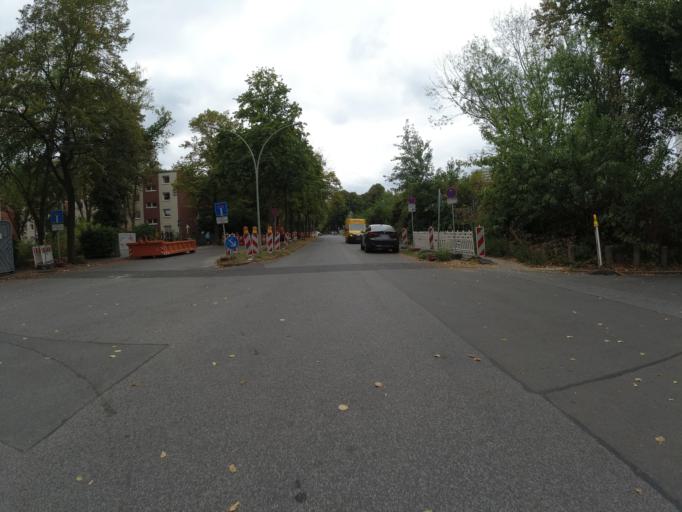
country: DE
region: North Rhine-Westphalia
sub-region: Regierungsbezirk Dusseldorf
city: Moers
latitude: 51.4520
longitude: 6.6936
